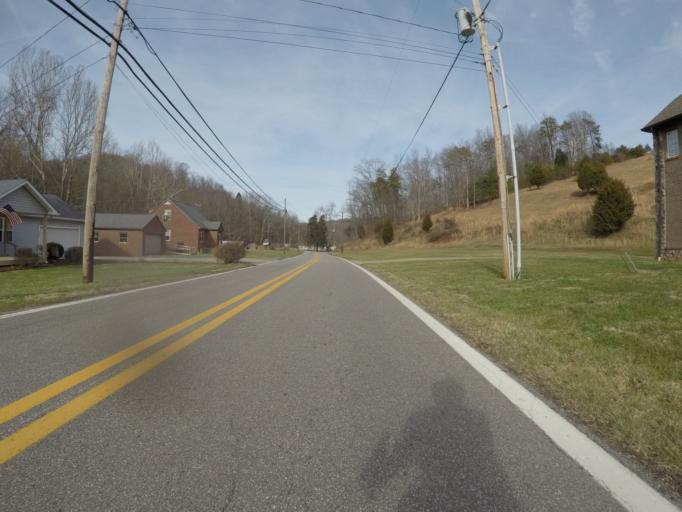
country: US
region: West Virginia
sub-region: Cabell County
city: Pea Ridge
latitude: 38.3600
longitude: -82.3714
